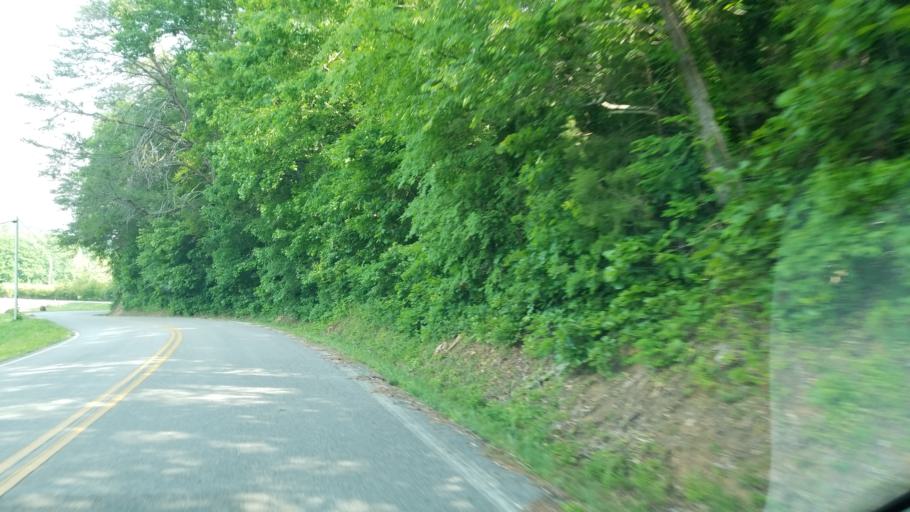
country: US
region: Tennessee
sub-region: Hamilton County
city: Collegedale
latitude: 35.0974
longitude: -85.0136
